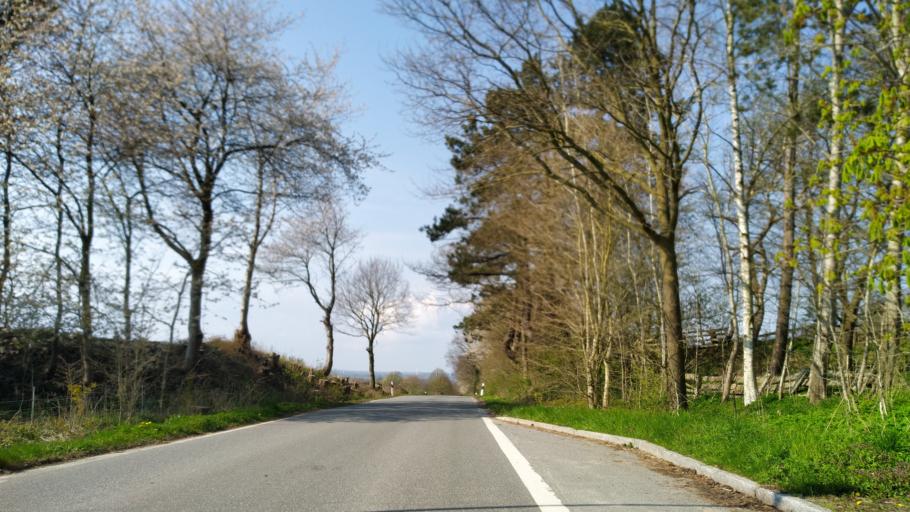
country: DE
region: Schleswig-Holstein
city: Bad Schwartau
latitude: 53.9432
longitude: 10.6795
